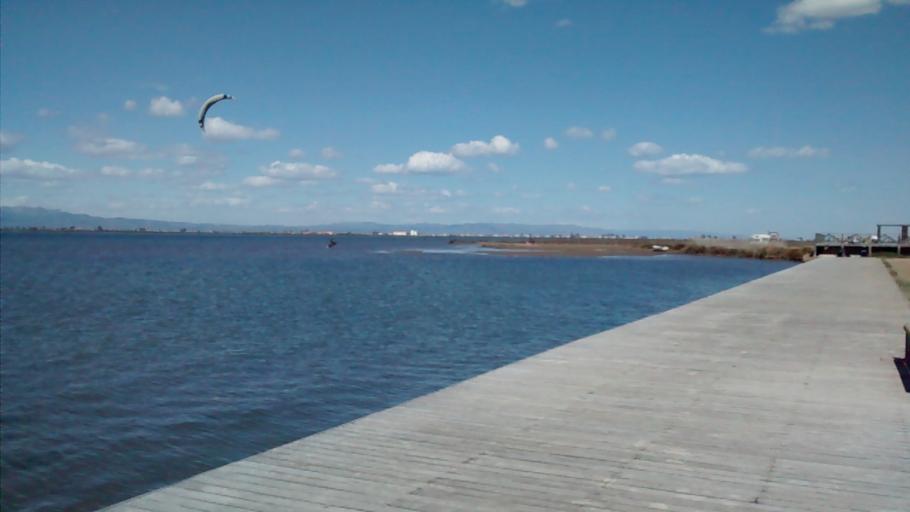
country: ES
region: Catalonia
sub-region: Provincia de Tarragona
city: Deltebre
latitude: 40.6287
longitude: 0.7410
